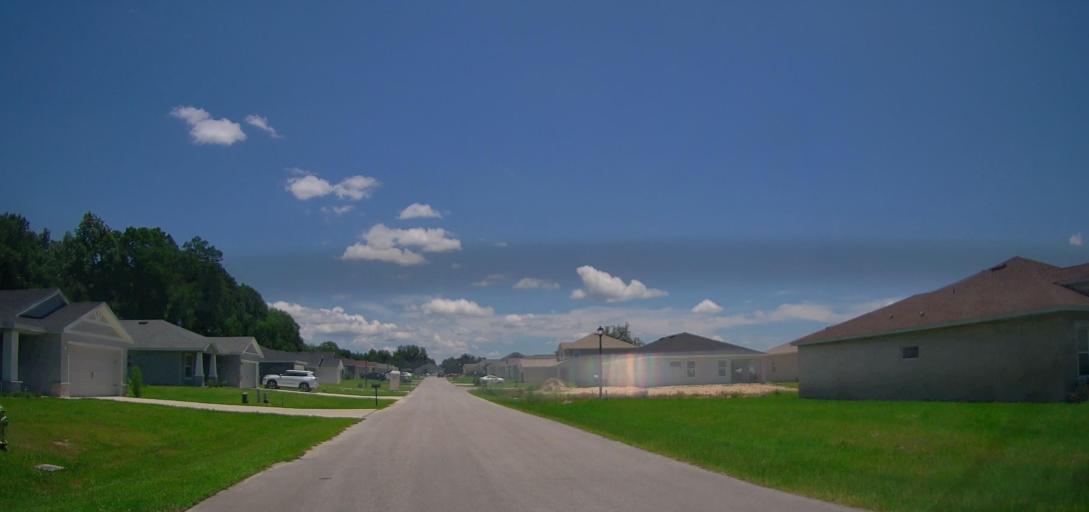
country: US
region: Florida
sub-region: Marion County
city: Belleview
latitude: 29.0930
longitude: -82.0671
